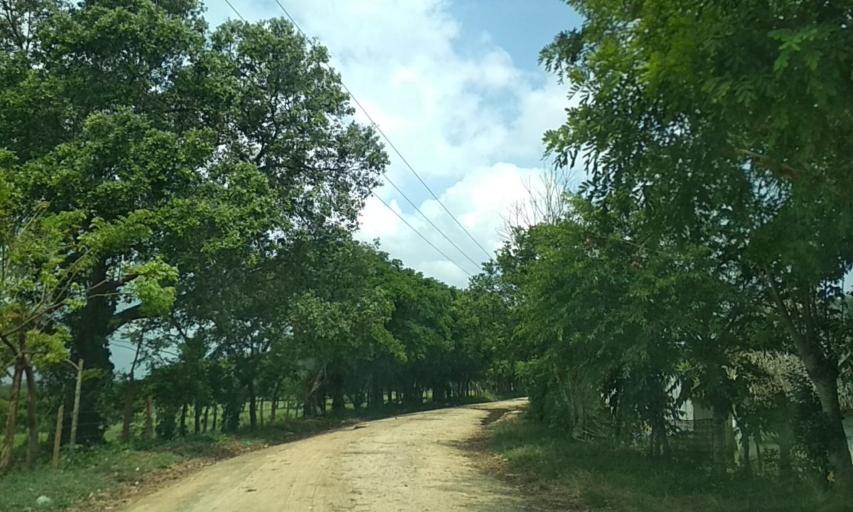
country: MX
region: Veracruz
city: Las Choapas
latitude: 17.8890
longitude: -94.1135
